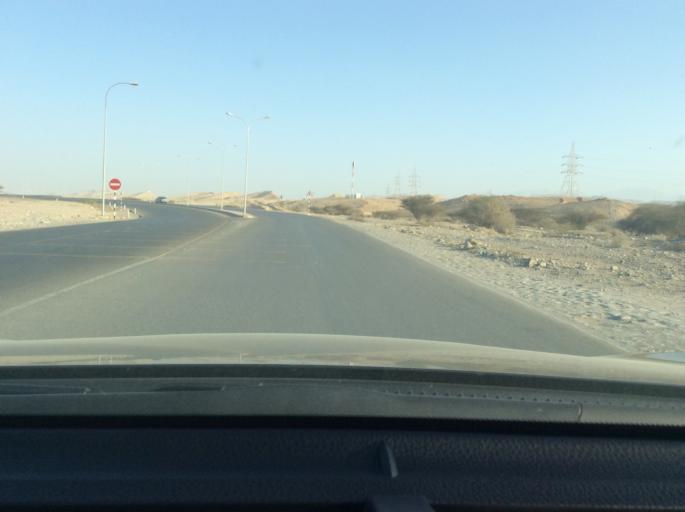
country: OM
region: Muhafazat Masqat
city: As Sib al Jadidah
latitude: 23.5735
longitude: 58.1867
